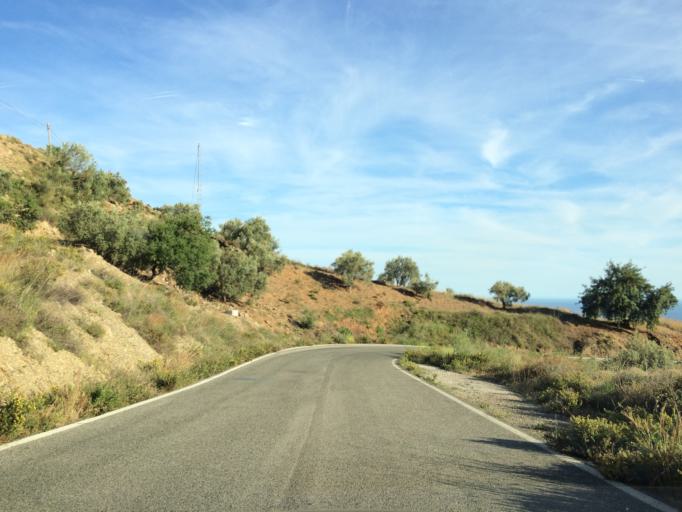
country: ES
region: Andalusia
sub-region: Provincia de Malaga
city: Totalan
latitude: 36.7490
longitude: -4.3313
